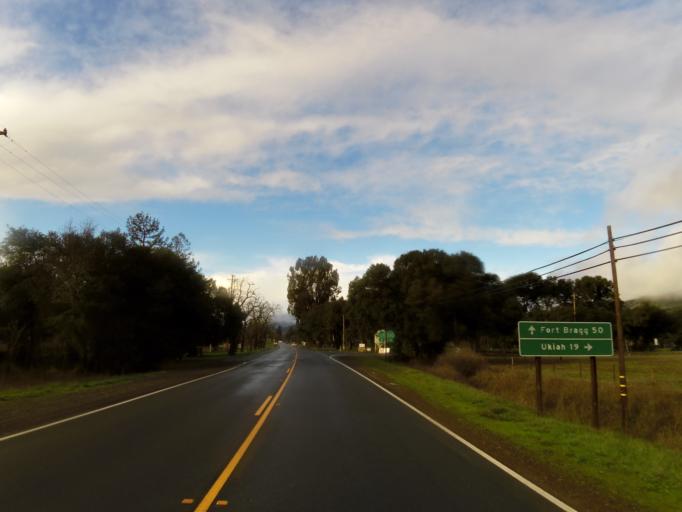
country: US
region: California
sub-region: Mendocino County
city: Boonville
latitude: 38.9984
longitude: -123.3578
